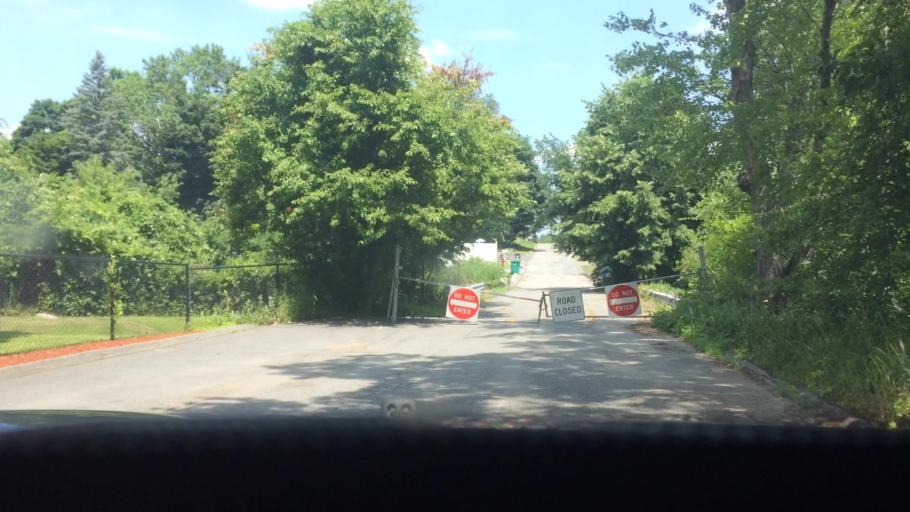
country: US
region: Massachusetts
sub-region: Middlesex County
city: Lowell
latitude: 42.6422
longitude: -71.3530
